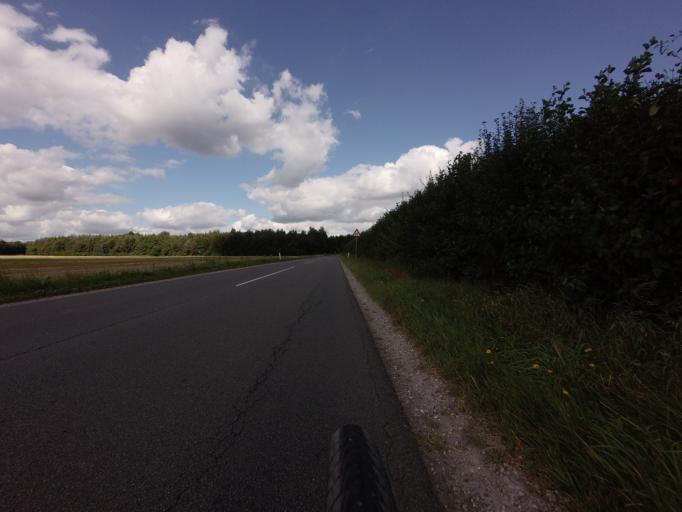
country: DK
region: Central Jutland
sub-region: Ikast-Brande Kommune
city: Brande
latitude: 55.9773
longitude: 9.1445
